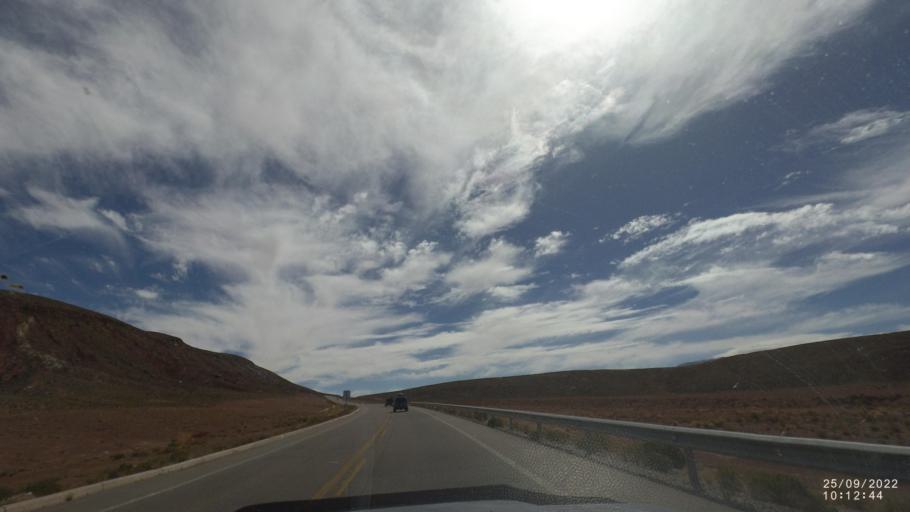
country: BO
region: Potosi
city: Colchani
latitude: -20.0824
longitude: -66.8912
